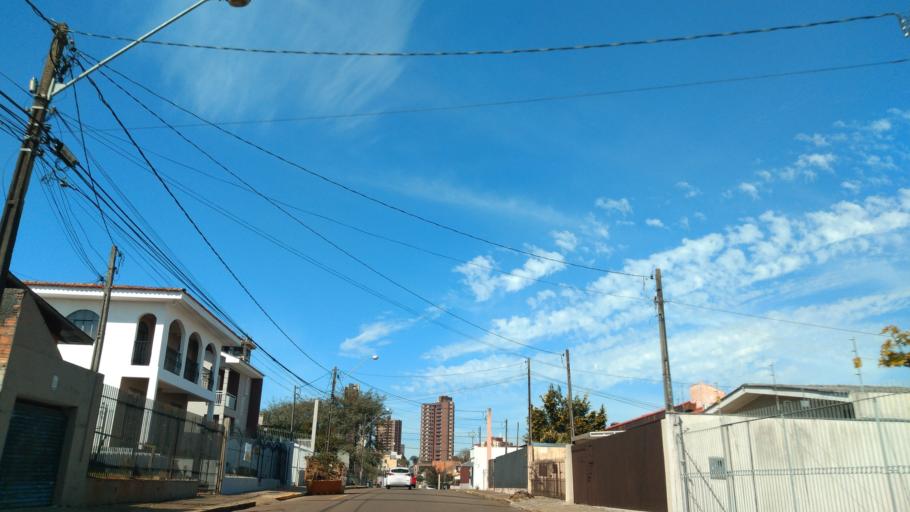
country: BR
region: Parana
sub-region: Guarapuava
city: Guarapuava
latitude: -25.3877
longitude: -51.4690
